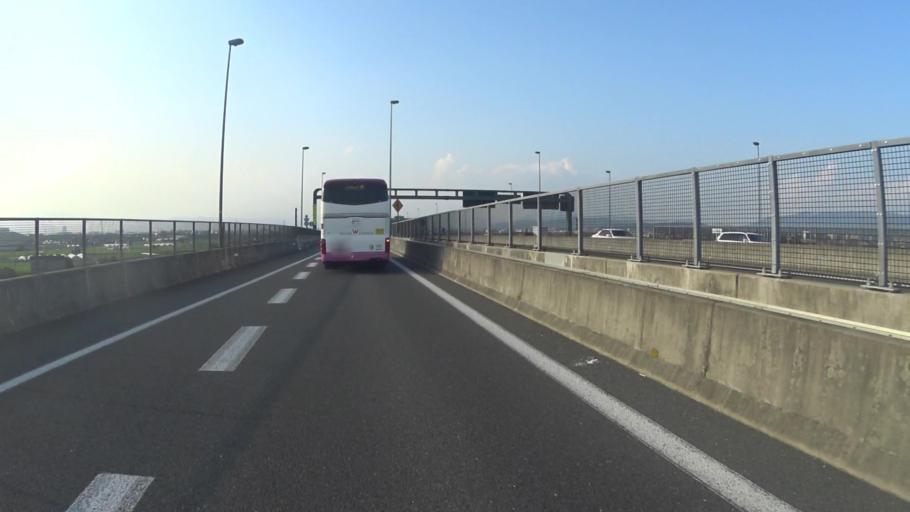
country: JP
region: Kyoto
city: Uji
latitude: 34.8996
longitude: 135.7493
